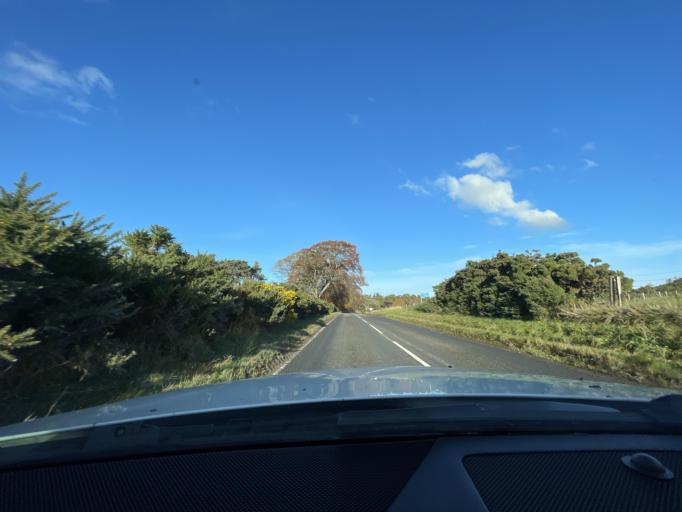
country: GB
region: Scotland
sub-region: Highland
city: Inverness
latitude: 57.3889
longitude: -4.3281
